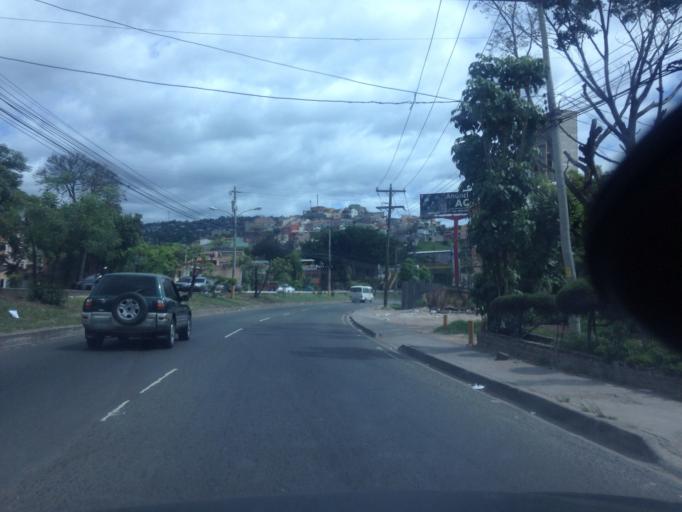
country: HN
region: Francisco Morazan
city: El Tablon
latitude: 14.0720
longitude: -87.1659
